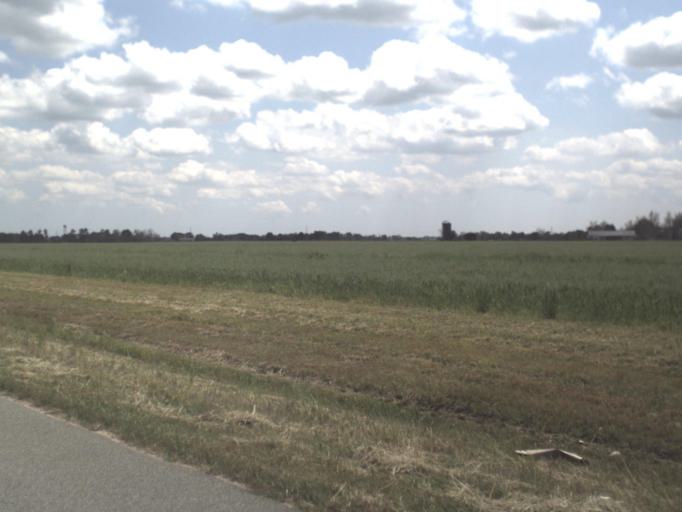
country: US
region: Florida
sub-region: Escambia County
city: Molino
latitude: 30.7378
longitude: -87.3566
